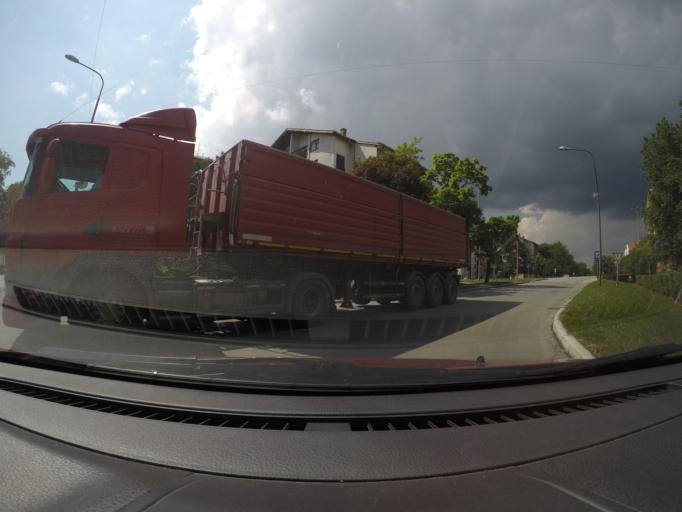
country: RS
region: Autonomna Pokrajina Vojvodina
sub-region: Srednjebanatski Okrug
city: Zrenjanin
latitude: 45.3811
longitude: 20.3741
